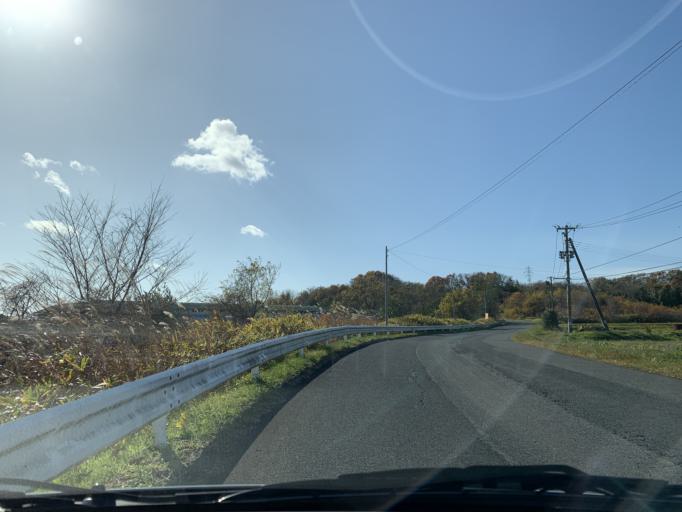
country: JP
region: Iwate
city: Mizusawa
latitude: 39.0323
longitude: 141.1132
